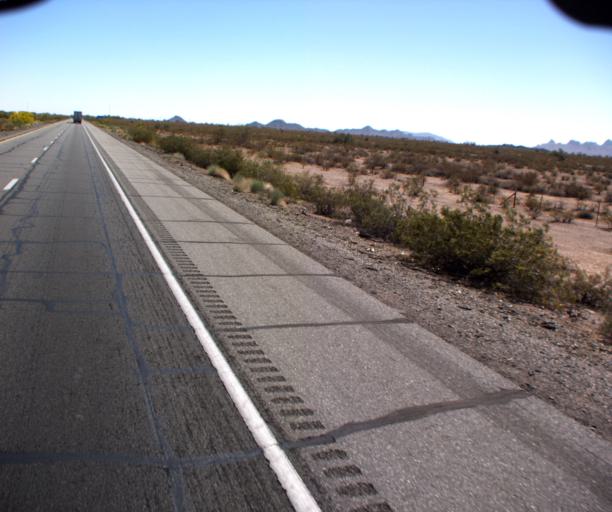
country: US
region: Arizona
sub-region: Maricopa County
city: Buckeye
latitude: 33.5230
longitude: -113.0859
